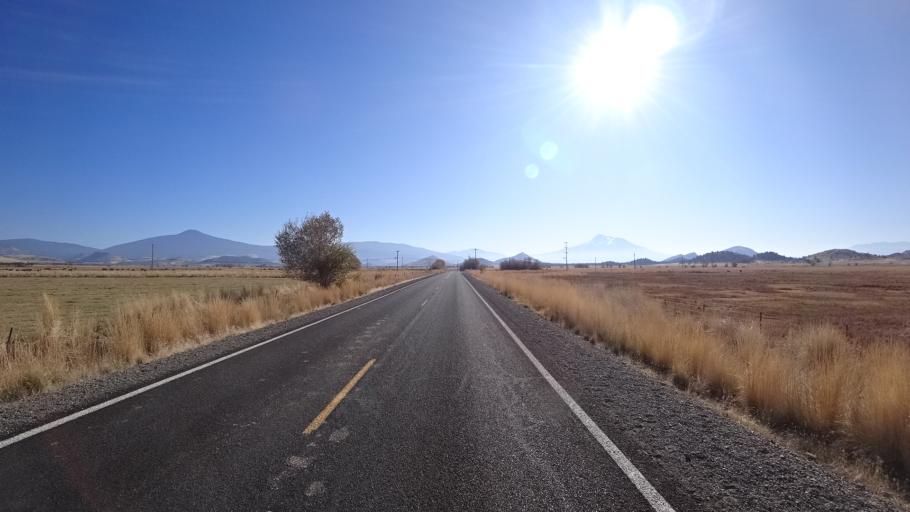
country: US
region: California
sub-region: Siskiyou County
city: Montague
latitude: 41.7129
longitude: -122.4394
